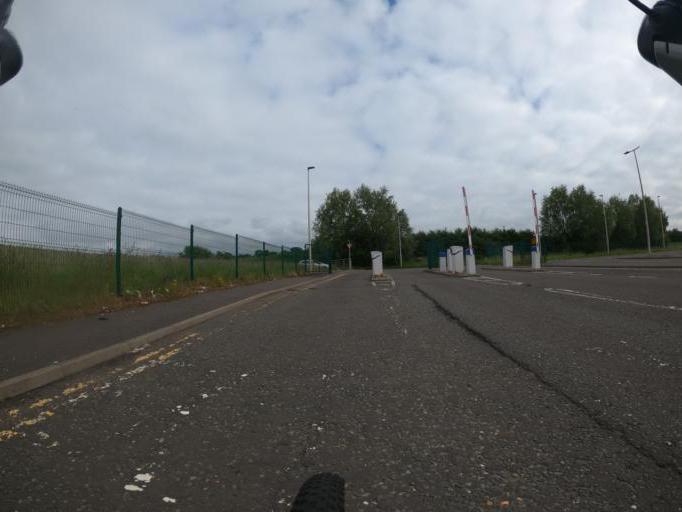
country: GB
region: Scotland
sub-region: Edinburgh
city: Ratho
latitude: 55.9389
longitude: -3.3543
